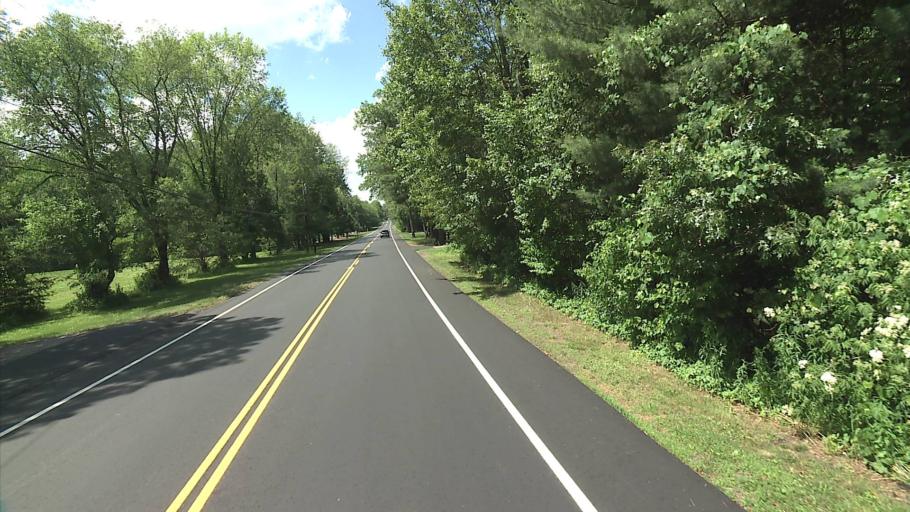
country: US
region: Connecticut
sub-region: Tolland County
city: Somers
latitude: 42.0119
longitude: -72.4435
